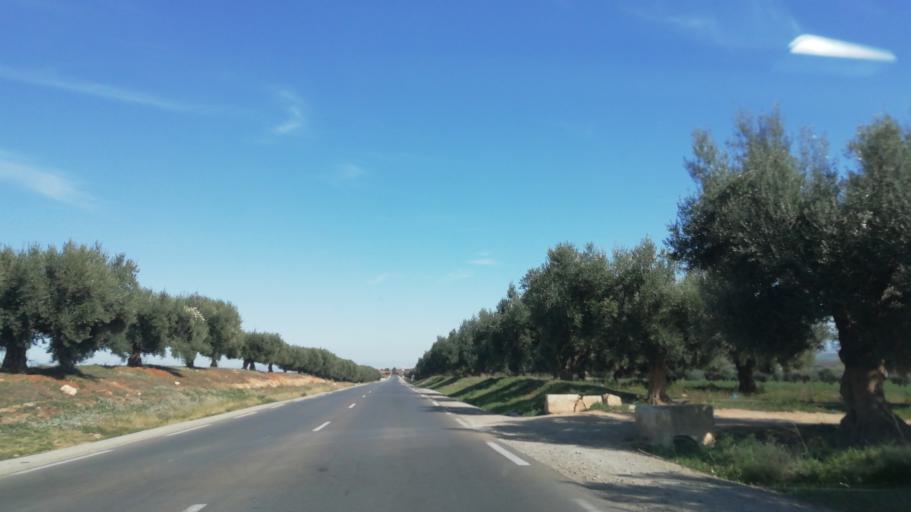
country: DZ
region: Mascara
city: Oued el Abtal
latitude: 35.4203
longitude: 0.4341
